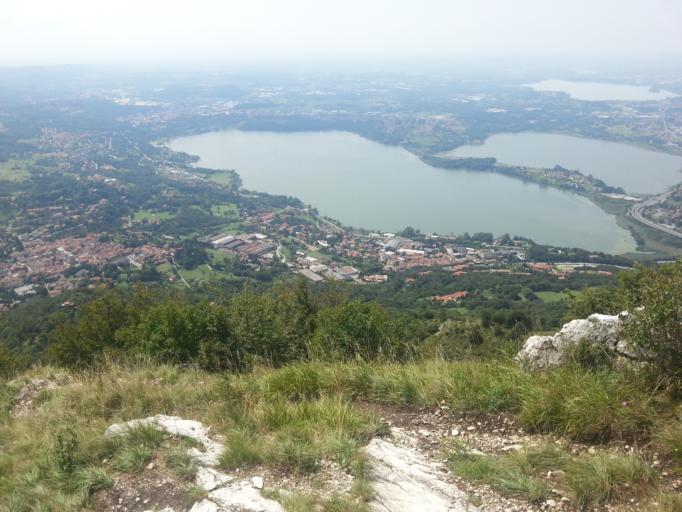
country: IT
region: Lombardy
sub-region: Provincia di Lecco
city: Pescate
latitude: 45.8308
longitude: 9.3801
